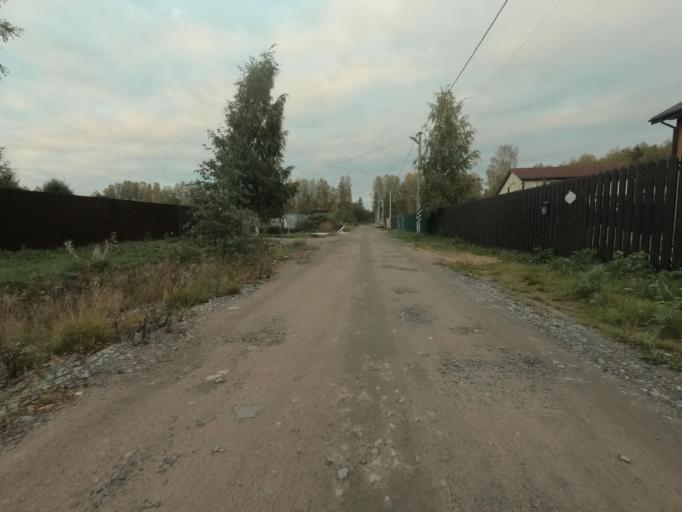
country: RU
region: Leningrad
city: Pavlovo
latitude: 59.8097
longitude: 30.9218
